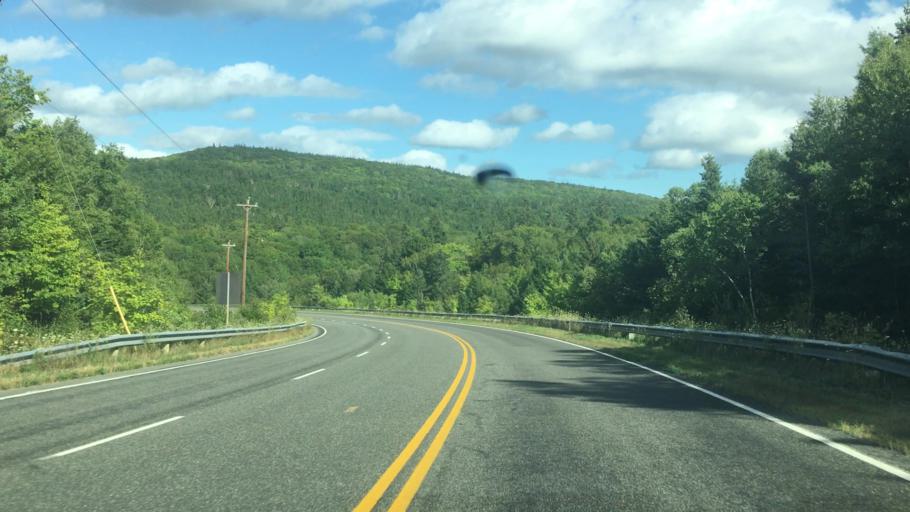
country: CA
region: Nova Scotia
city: Sydney
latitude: 45.8133
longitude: -60.6755
